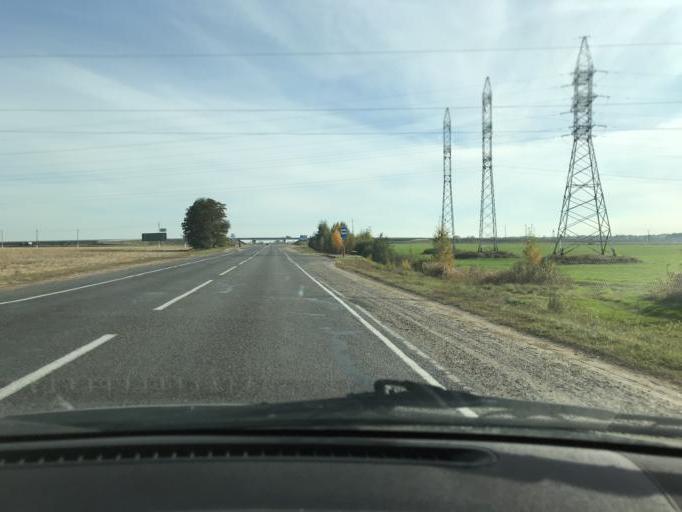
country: BY
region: Brest
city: Asnyezhytsy
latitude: 52.1895
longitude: 26.0753
